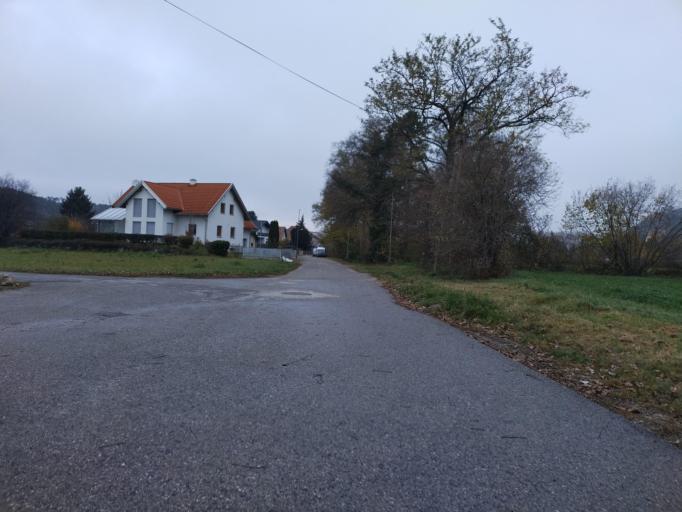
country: AT
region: Lower Austria
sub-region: Politischer Bezirk Neunkirchen
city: Pitten
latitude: 47.7106
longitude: 16.1756
